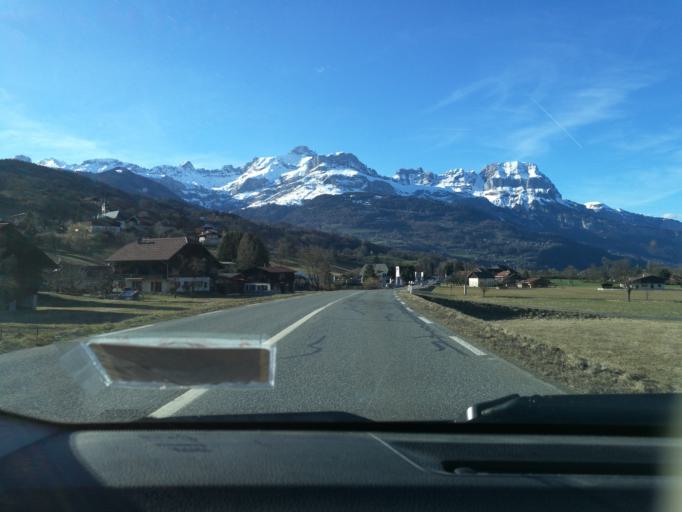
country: FR
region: Rhone-Alpes
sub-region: Departement de la Haute-Savoie
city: Domancy
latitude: 45.9120
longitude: 6.6544
